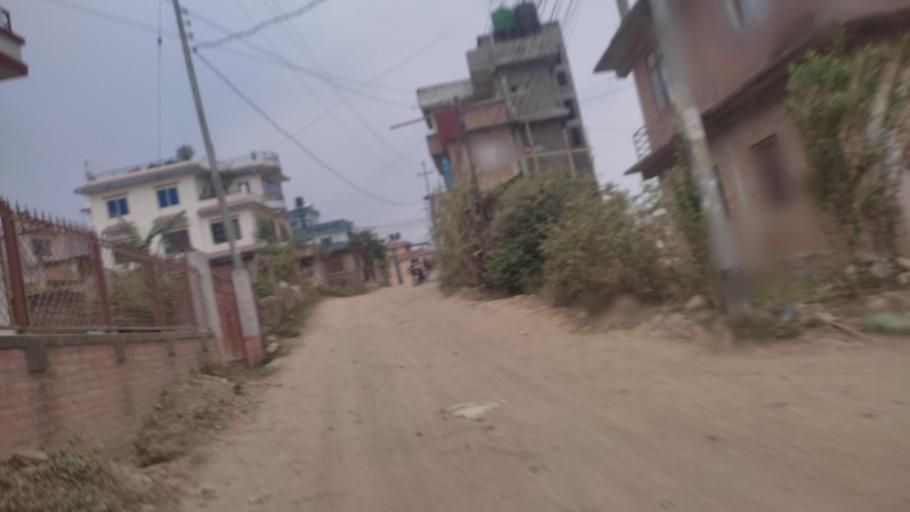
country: NP
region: Central Region
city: Kirtipur
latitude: 27.6639
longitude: 85.2707
